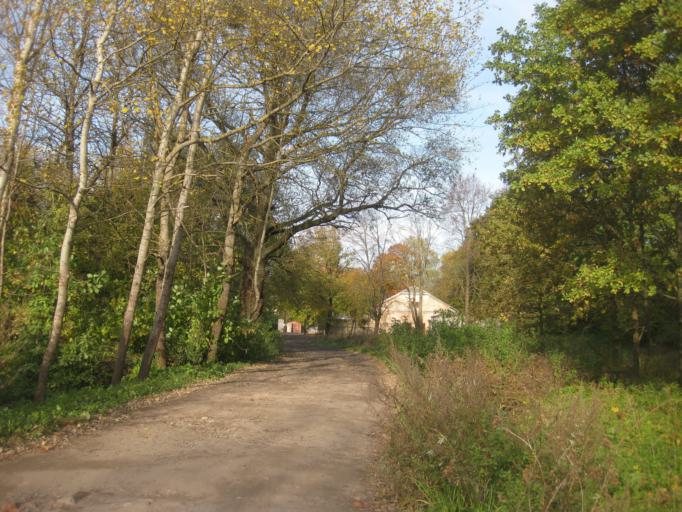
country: LT
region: Kauno apskritis
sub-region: Kaunas
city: Aleksotas
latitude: 54.8898
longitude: 23.8809
